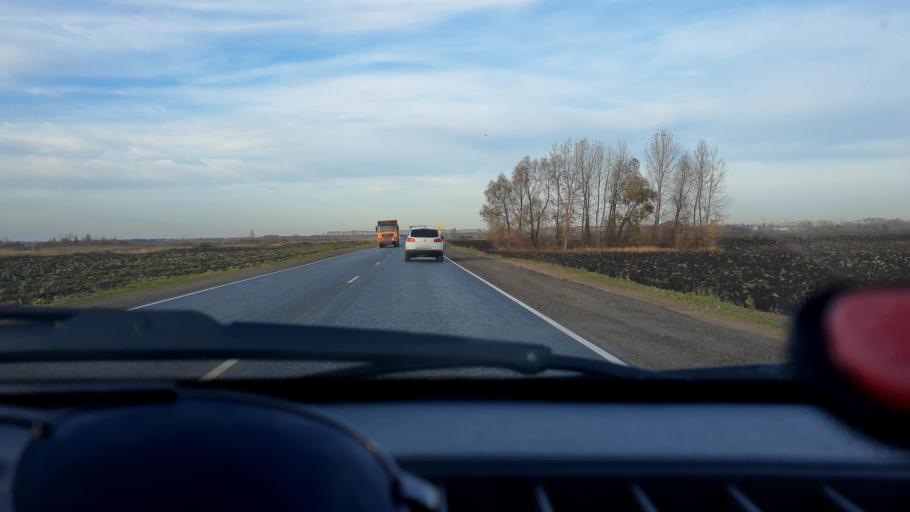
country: RU
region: Bashkortostan
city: Ufa
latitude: 54.8050
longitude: 55.9642
